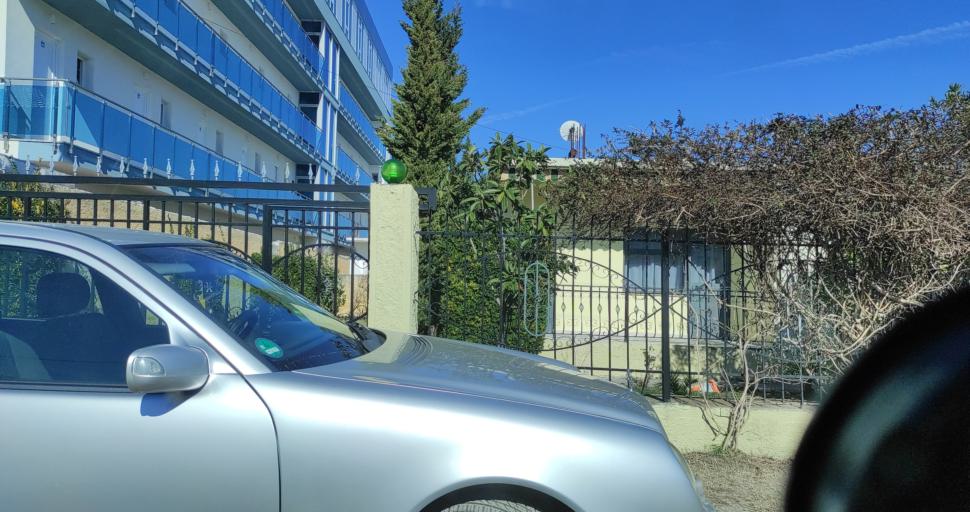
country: AL
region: Shkoder
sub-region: Rrethi i Shkodres
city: Velipoje
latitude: 41.8664
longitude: 19.4247
